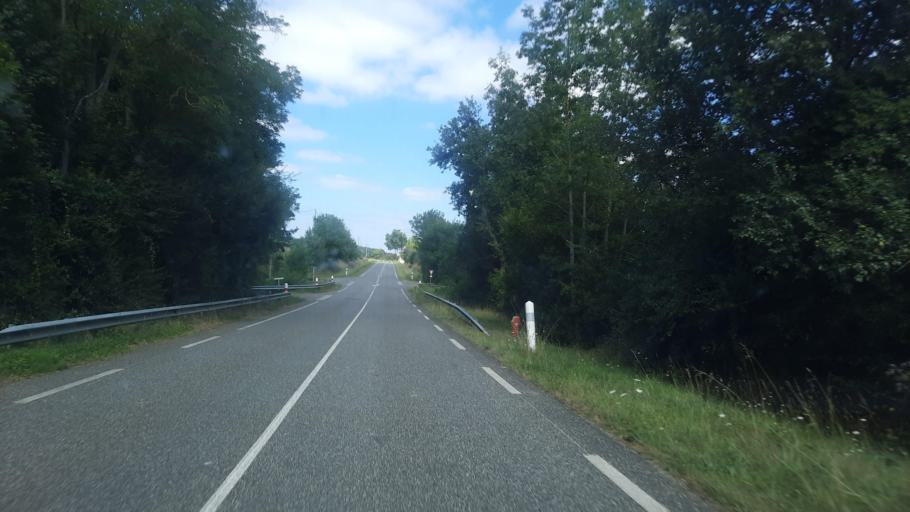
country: FR
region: Midi-Pyrenees
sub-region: Departement du Gers
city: Lombez
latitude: 43.3912
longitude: 0.7839
